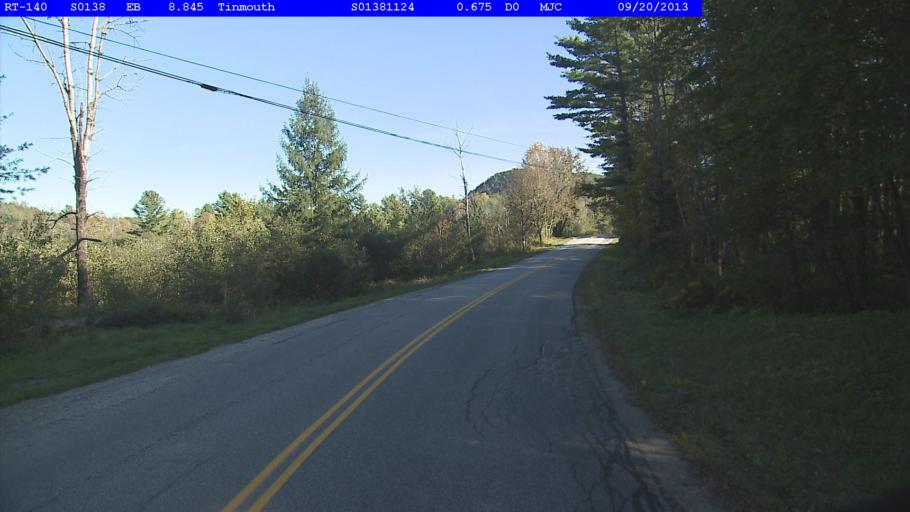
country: US
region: Vermont
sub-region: Rutland County
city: West Rutland
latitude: 43.4777
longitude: -73.0666
